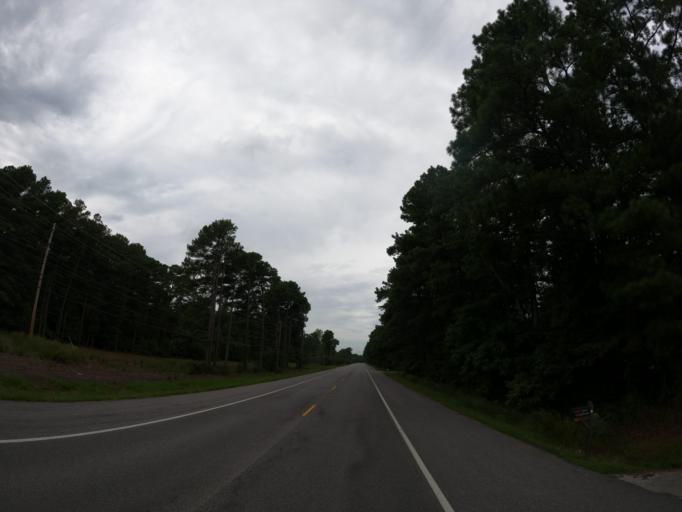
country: US
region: Maryland
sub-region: Saint Mary's County
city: Lexington Park
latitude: 38.1599
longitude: -76.5250
